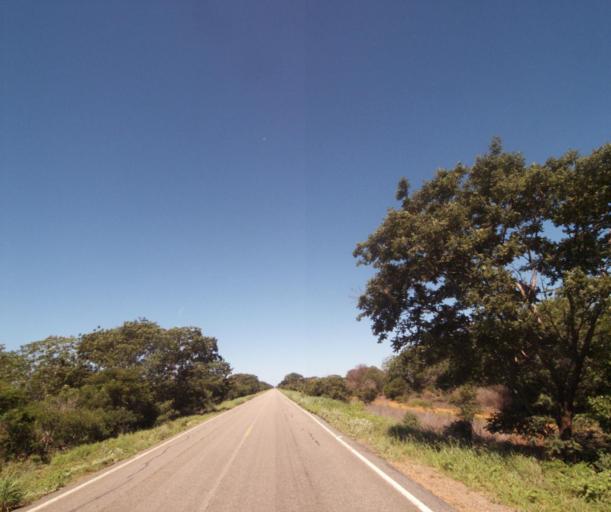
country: BR
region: Bahia
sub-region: Palmas De Monte Alto
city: Palmas de Monte Alto
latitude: -14.2624
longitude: -43.3211
